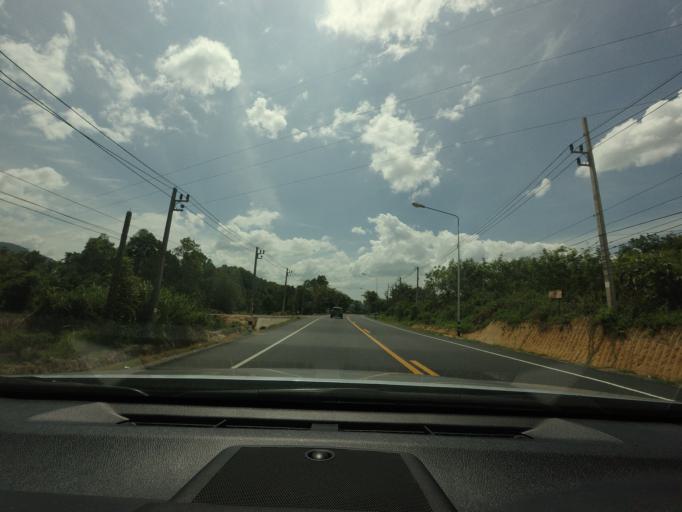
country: TH
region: Yala
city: Krong Pi Nang
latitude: 6.4673
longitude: 101.3274
